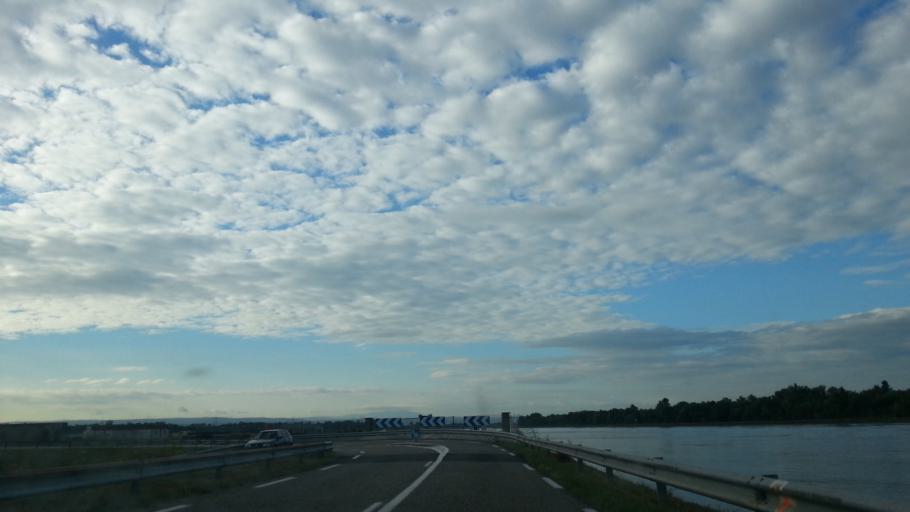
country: FR
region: Alsace
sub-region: Departement du Bas-Rhin
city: Gerstheim
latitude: 48.3666
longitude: 7.7282
